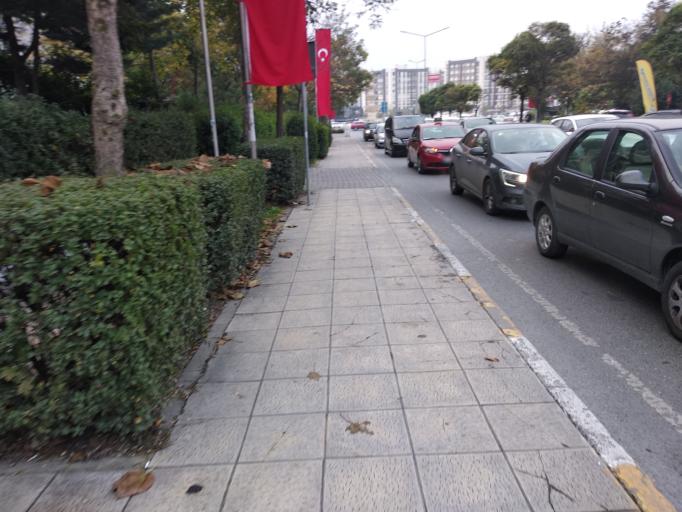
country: TR
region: Istanbul
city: Beylikduezue
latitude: 41.0048
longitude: 28.6380
